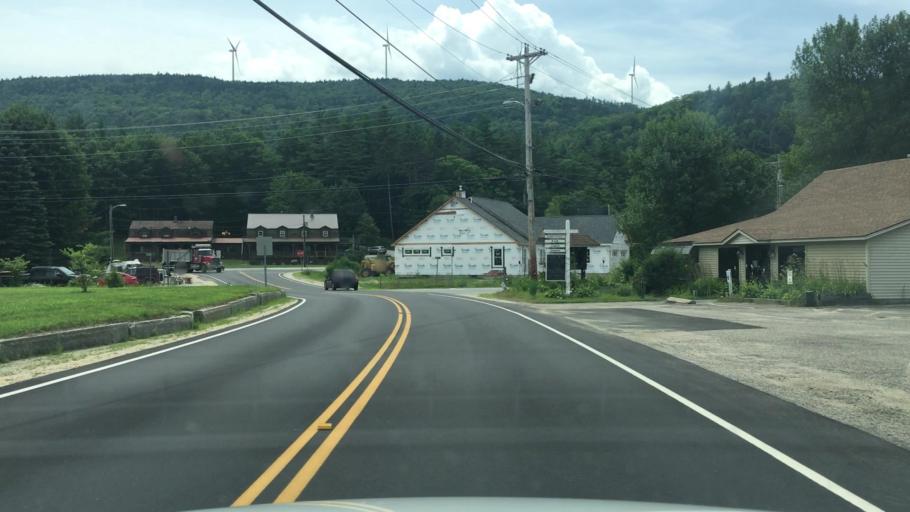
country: US
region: New Hampshire
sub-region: Grafton County
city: Rumney
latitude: 43.7960
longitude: -71.8168
